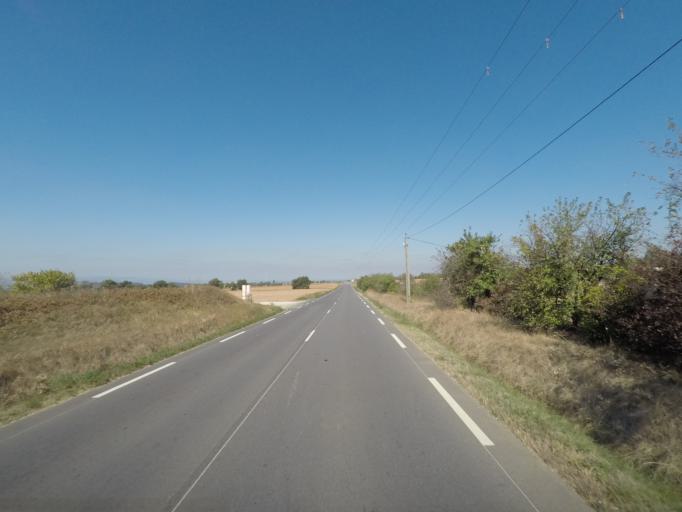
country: FR
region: Rhone-Alpes
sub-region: Departement de la Drome
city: Upie
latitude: 44.8122
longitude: 5.0123
